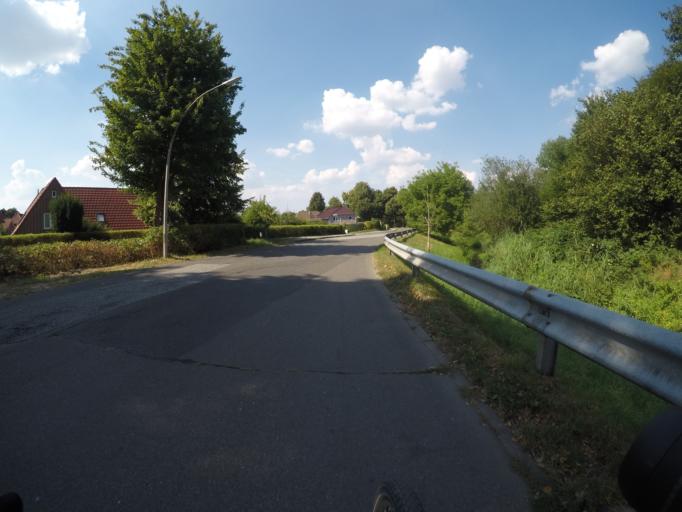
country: DE
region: Hamburg
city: Bergedorf
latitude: 53.4827
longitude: 10.1941
